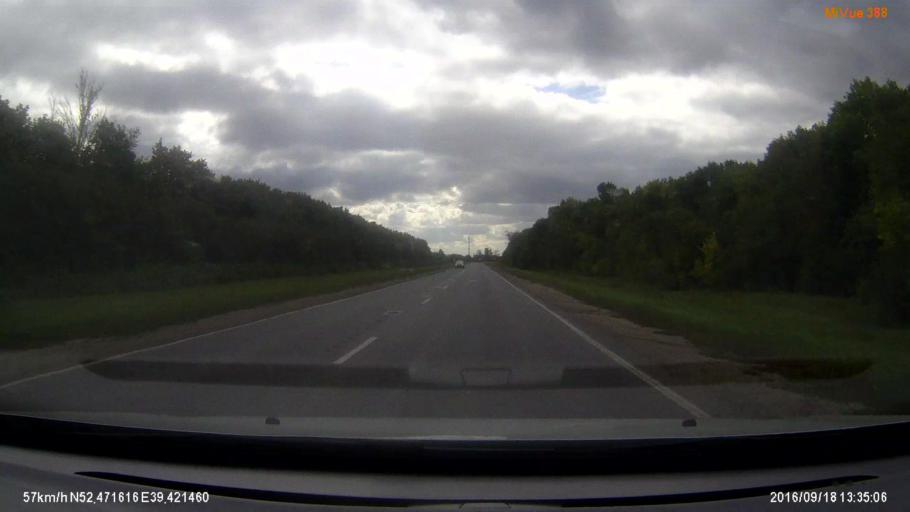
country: RU
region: Lipetsk
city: Borinskoye
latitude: 52.4947
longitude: 39.4504
